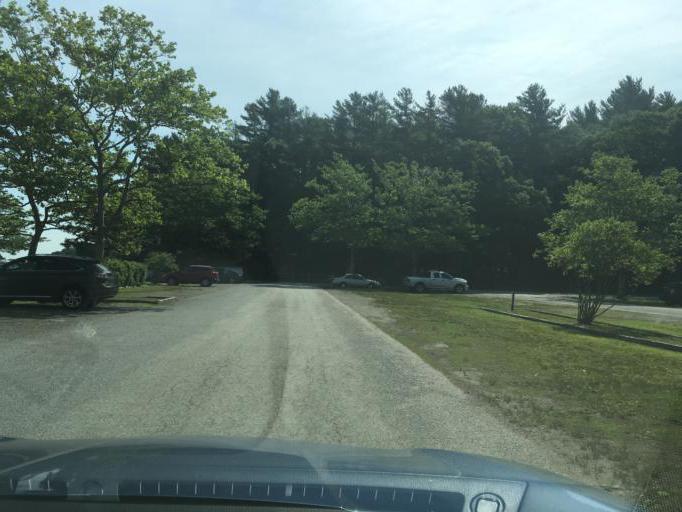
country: US
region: Rhode Island
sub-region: Kent County
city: East Greenwich
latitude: 41.6663
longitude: -71.4335
